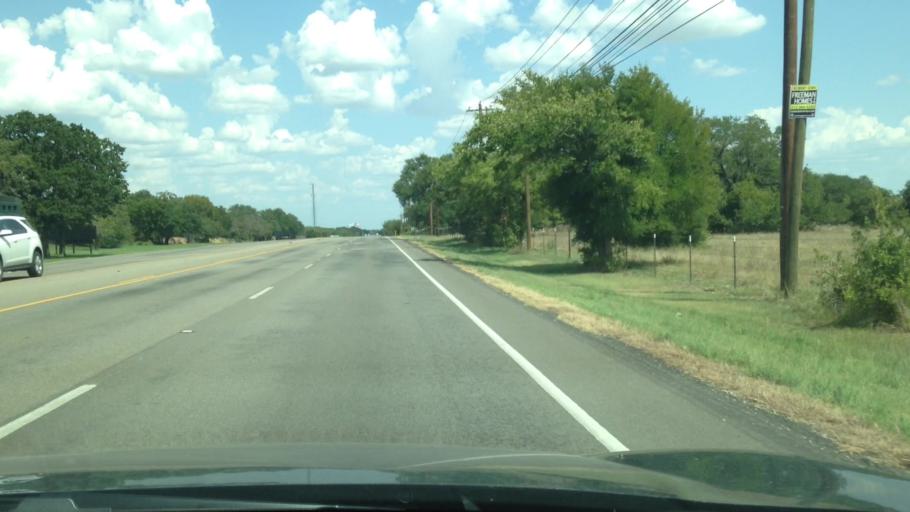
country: US
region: Texas
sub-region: Williamson County
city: Leander
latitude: 30.6354
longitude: -97.7856
